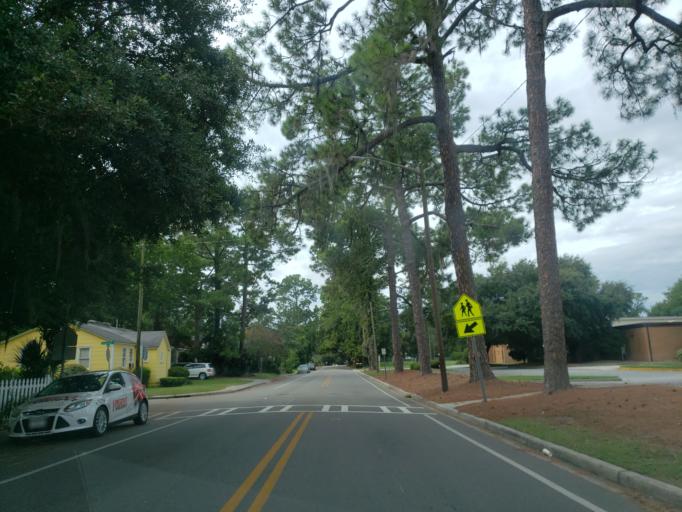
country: US
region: Georgia
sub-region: Chatham County
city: Thunderbolt
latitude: 32.0616
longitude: -81.0663
